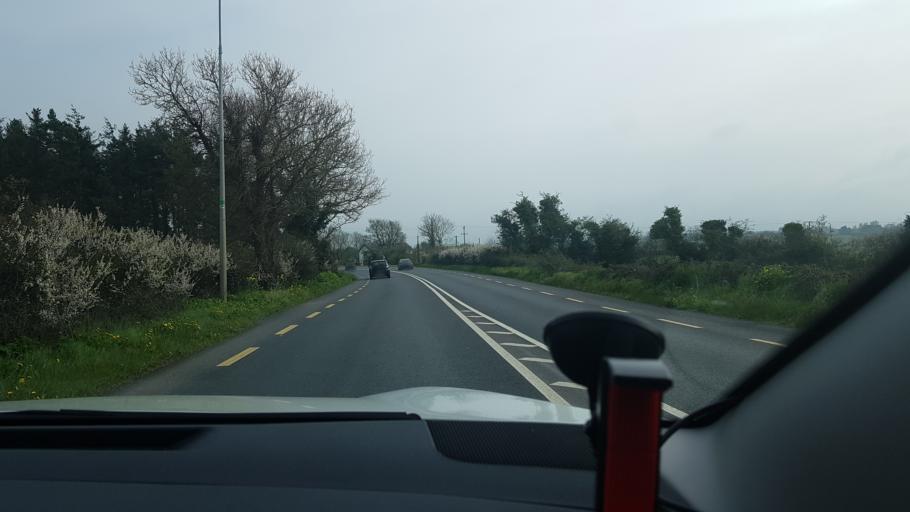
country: IE
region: Leinster
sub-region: An Mhi
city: Stamullin
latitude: 53.6632
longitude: -6.2716
